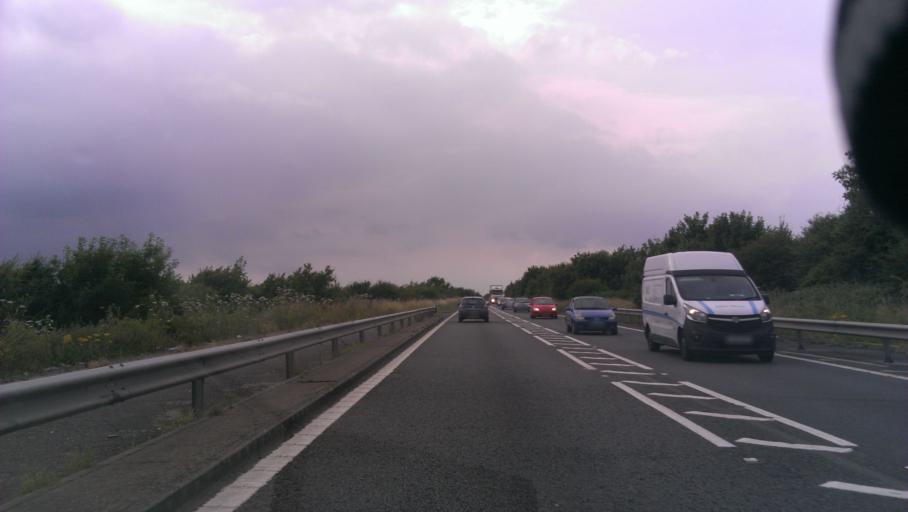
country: GB
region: England
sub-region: Kent
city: Dover
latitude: 51.1590
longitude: 1.2745
